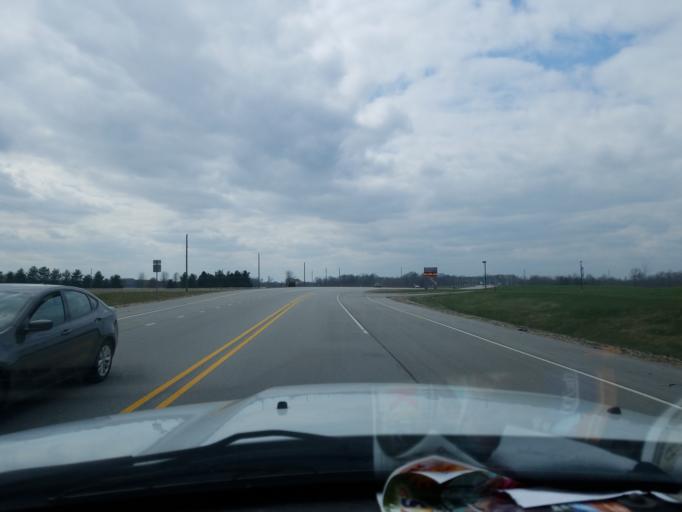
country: US
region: Indiana
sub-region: Vigo County
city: Terre Haute
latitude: 39.4085
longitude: -87.3287
